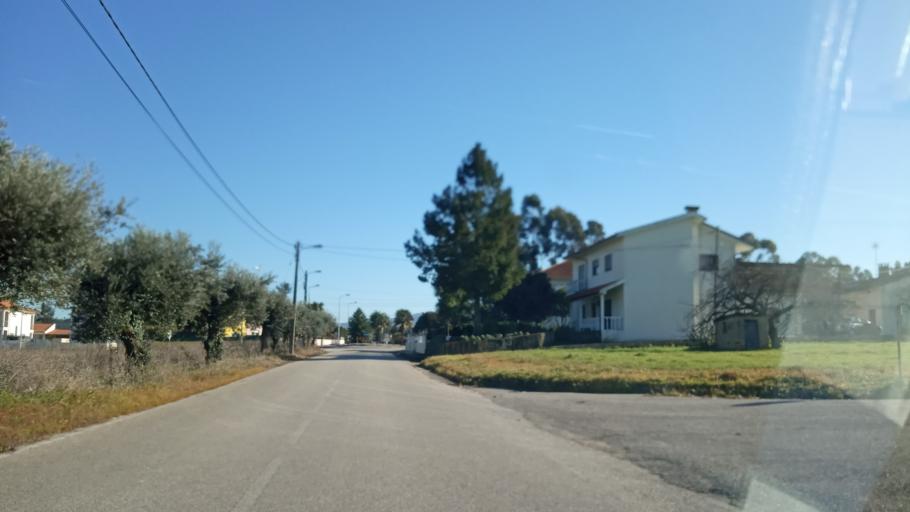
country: PT
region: Aveiro
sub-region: Anadia
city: Anadia
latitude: 40.4261
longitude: -8.4266
